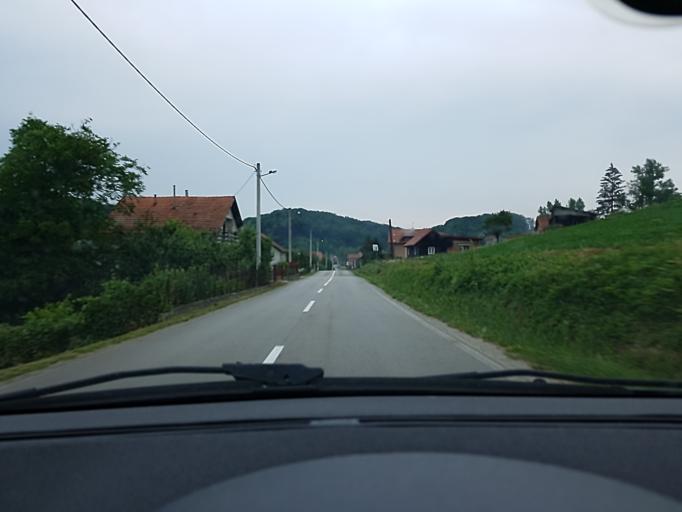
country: HR
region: Zagrebacka
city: Jakovlje
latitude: 45.9747
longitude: 15.8328
